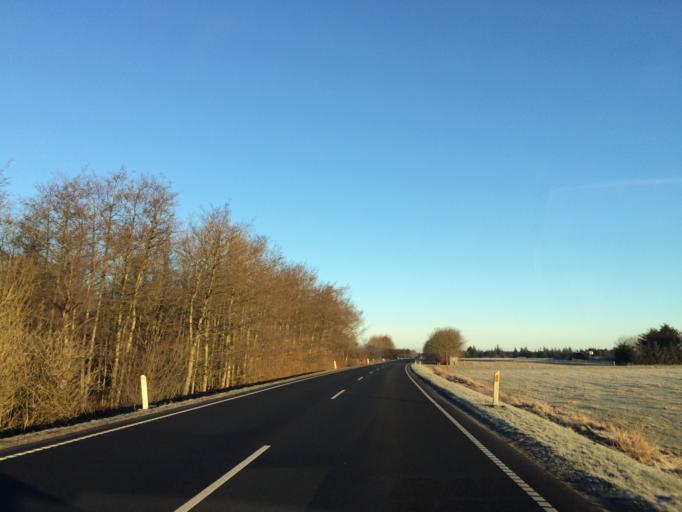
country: DK
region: Central Jutland
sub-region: Holstebro Kommune
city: Ulfborg
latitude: 56.3533
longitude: 8.3387
